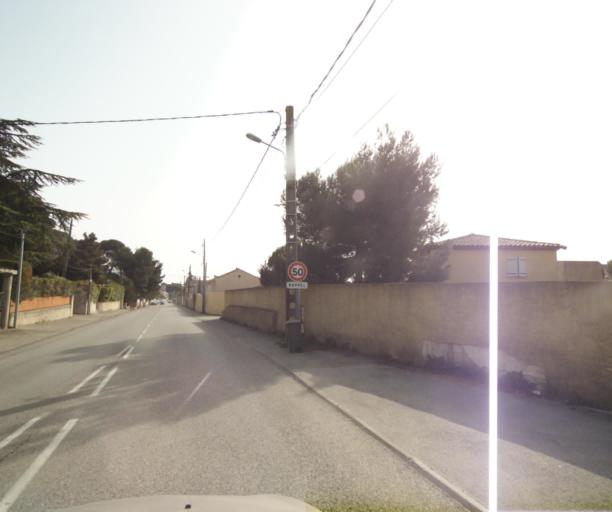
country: FR
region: Provence-Alpes-Cote d'Azur
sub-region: Departement des Bouches-du-Rhone
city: Marseille 15
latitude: 43.3907
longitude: 5.3439
